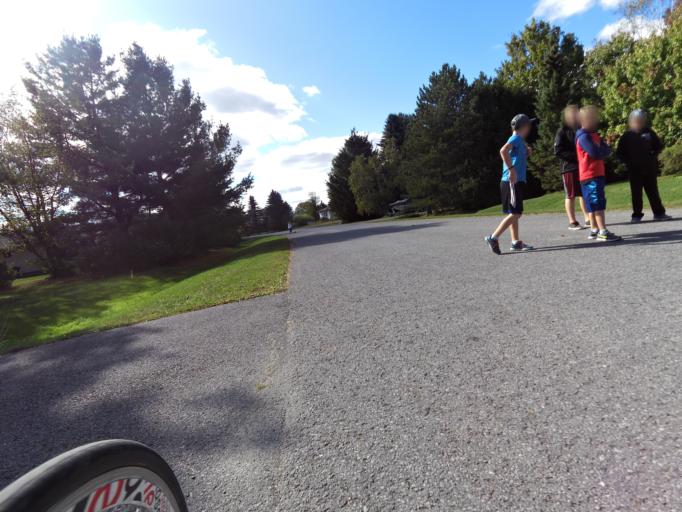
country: CA
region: Ontario
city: Bells Corners
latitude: 45.1543
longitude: -75.6534
